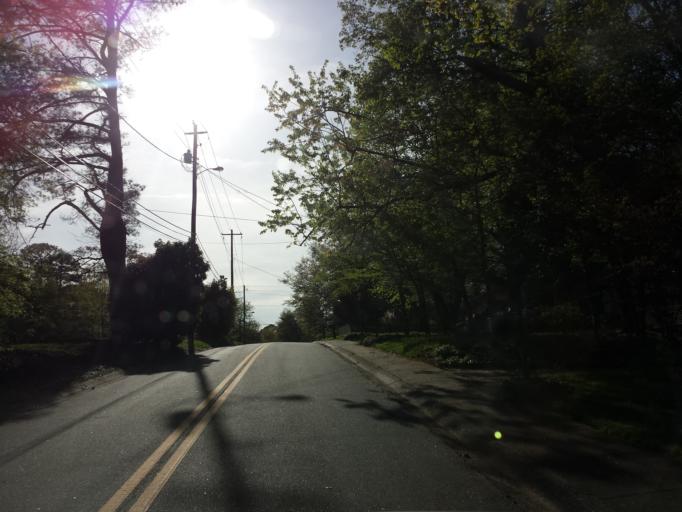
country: US
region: Georgia
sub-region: Cobb County
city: Marietta
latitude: 33.9574
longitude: -84.5644
